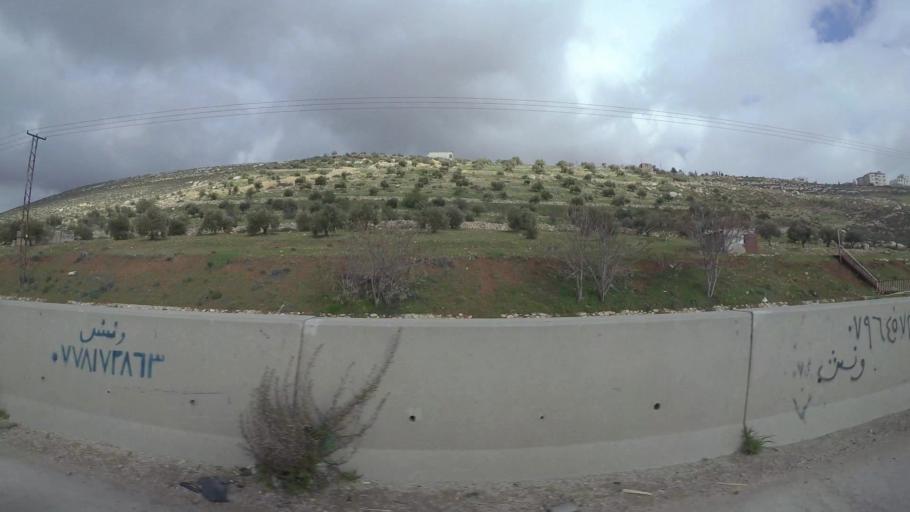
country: JO
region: Amman
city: Al Jubayhah
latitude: 32.0768
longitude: 35.8786
